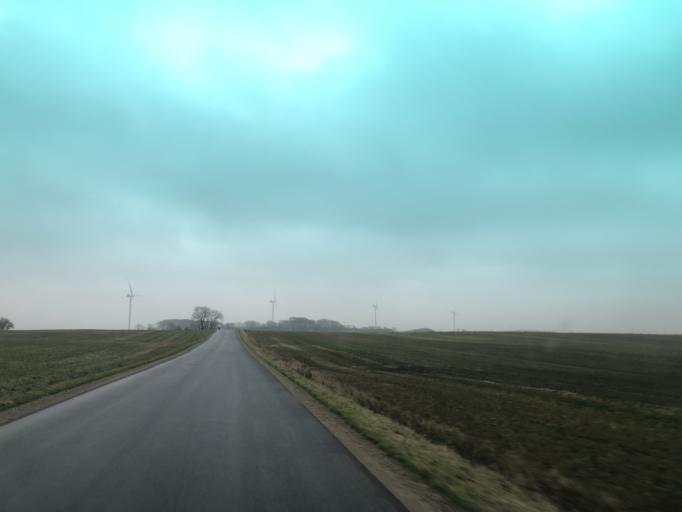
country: DK
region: Central Jutland
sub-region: Struer Kommune
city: Struer
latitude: 56.4332
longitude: 8.5873
